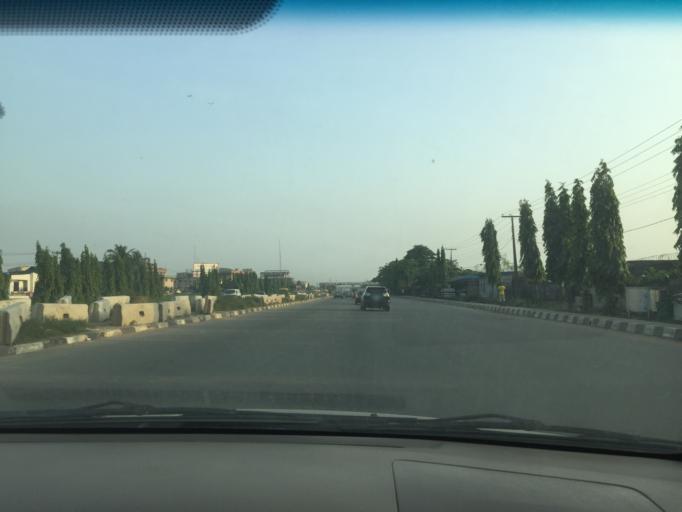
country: NG
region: Lagos
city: Ikeja
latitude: 6.5986
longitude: 3.3343
